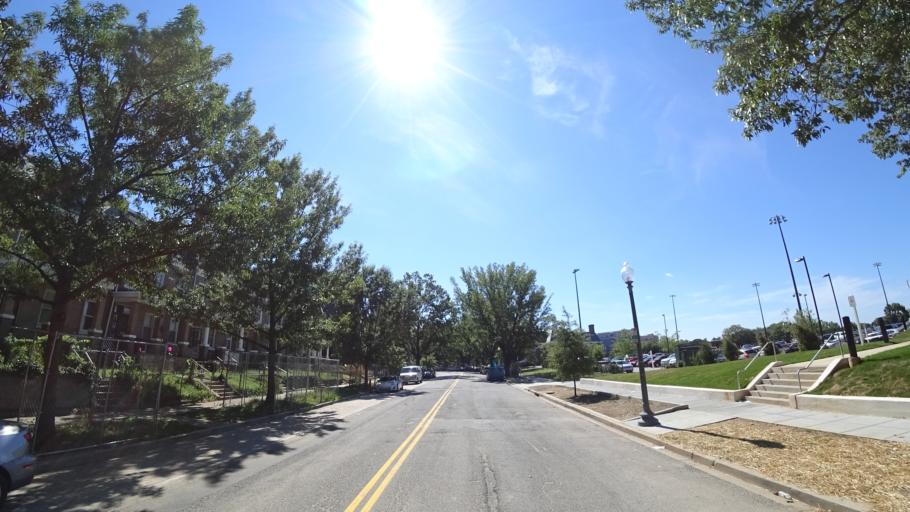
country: US
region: Maryland
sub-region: Montgomery County
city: Takoma Park
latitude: 38.9437
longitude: -77.0270
